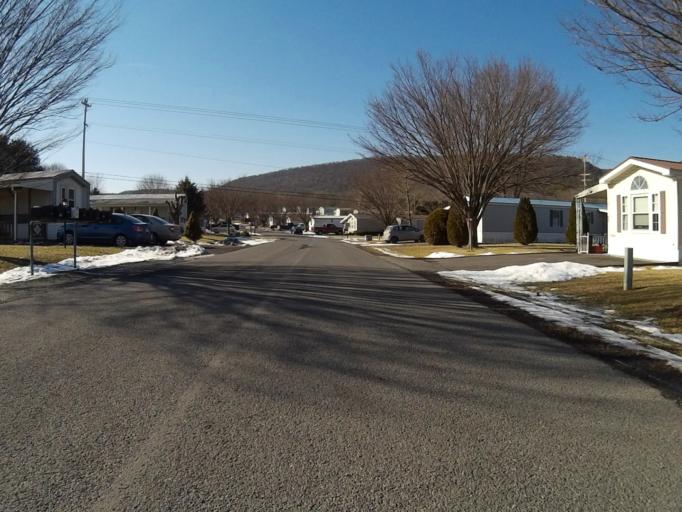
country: US
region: Pennsylvania
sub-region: Centre County
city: Houserville
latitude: 40.8727
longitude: -77.8661
